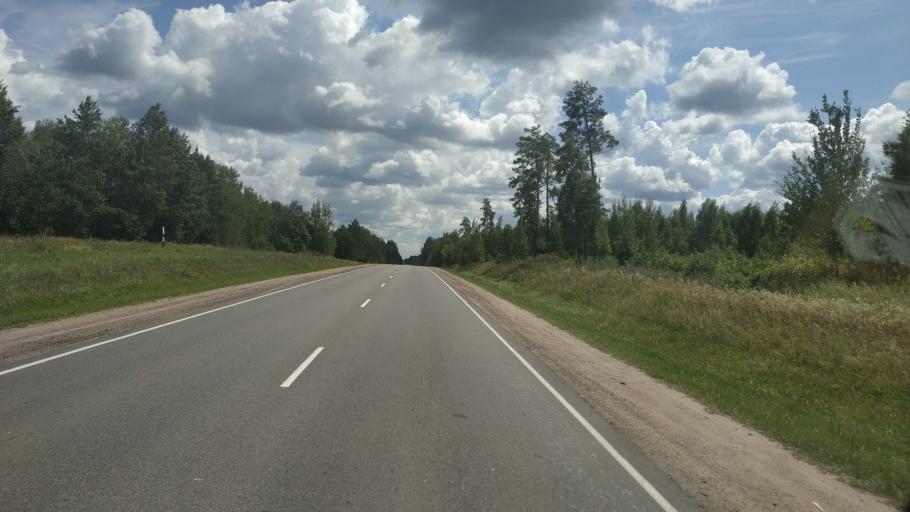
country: BY
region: Mogilev
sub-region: Mahilyowski Rayon
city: Veyno
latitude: 53.8269
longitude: 30.4179
